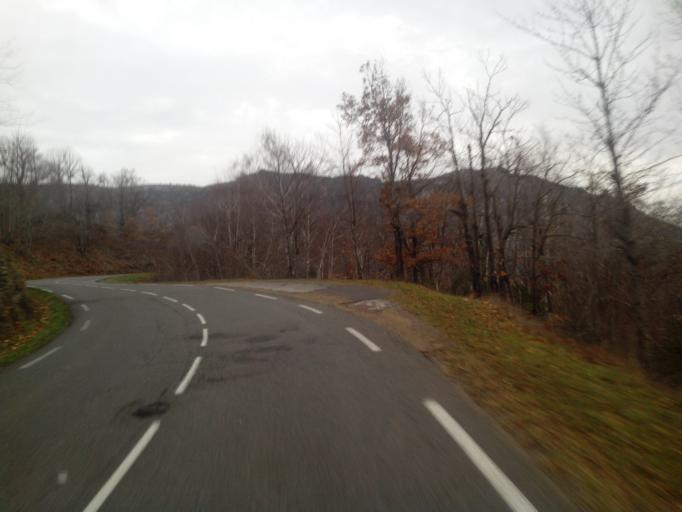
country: FR
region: Languedoc-Roussillon
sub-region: Departement de la Lozere
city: Florac
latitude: 44.2788
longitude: 3.5973
